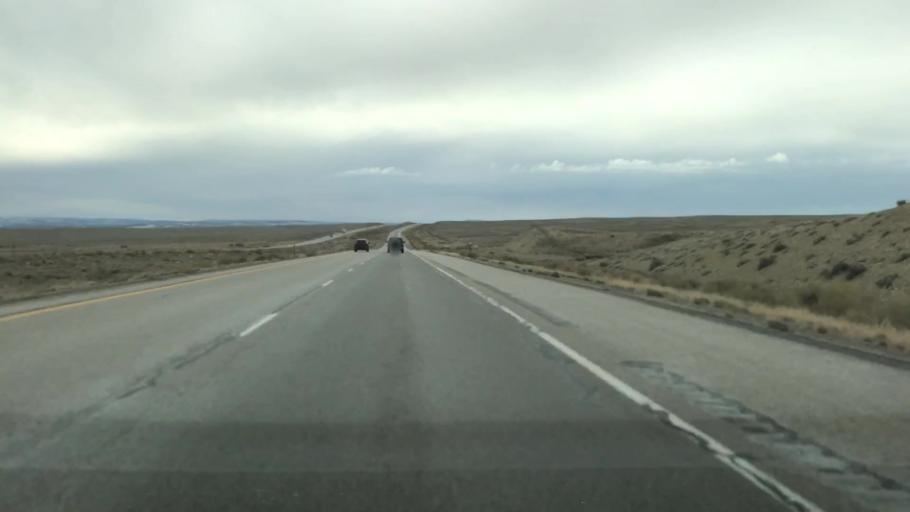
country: US
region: Utah
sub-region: Grand County
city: Moab
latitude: 39.0192
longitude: -109.3012
